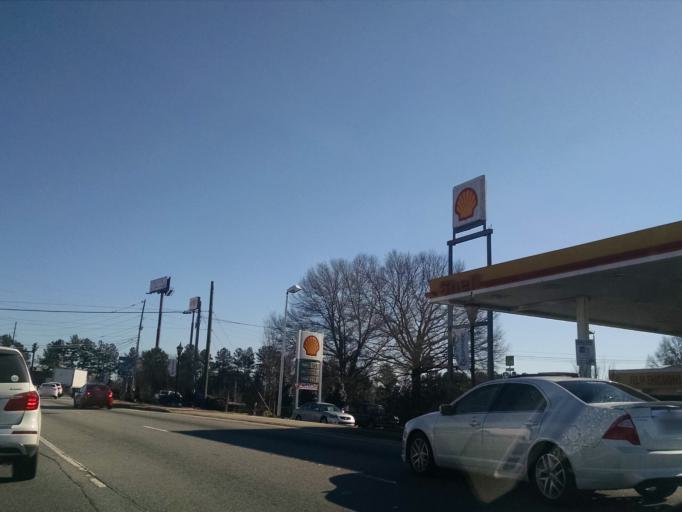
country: US
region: Georgia
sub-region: Gwinnett County
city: Suwanee
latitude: 34.0311
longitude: -84.0495
